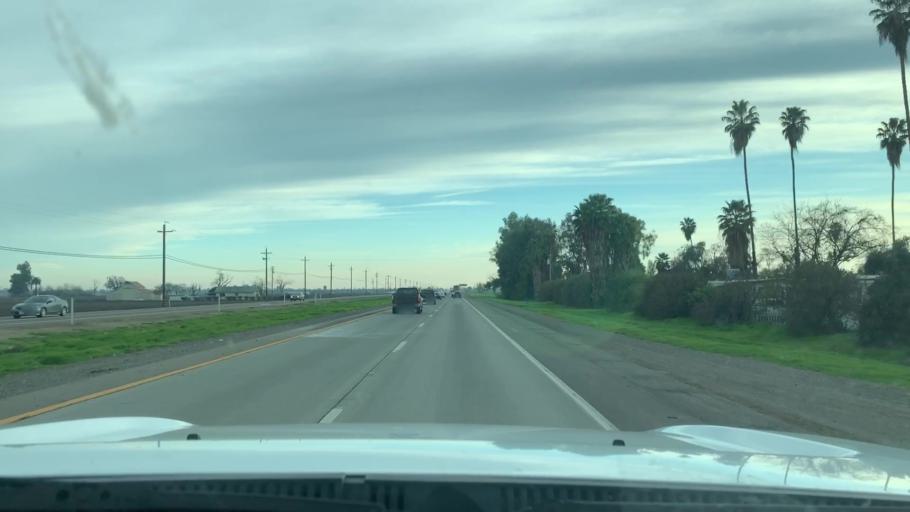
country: US
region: California
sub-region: Kings County
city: Lemoore
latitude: 36.3329
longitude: -119.8082
